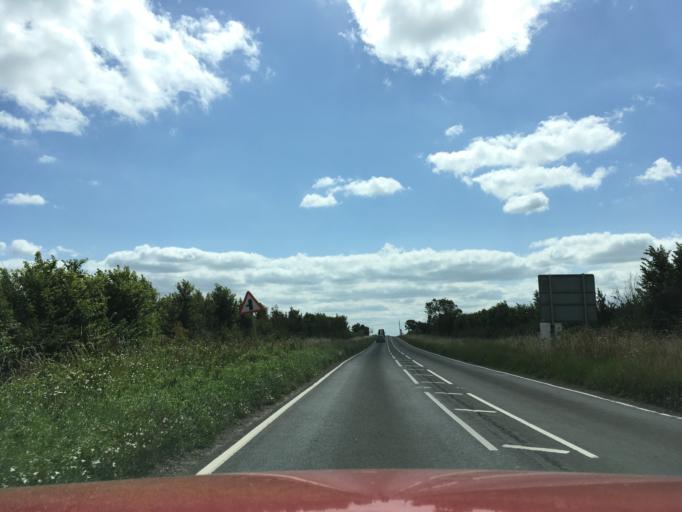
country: GB
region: England
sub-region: Buckinghamshire
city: Winslow
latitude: 51.9172
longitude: -0.8419
